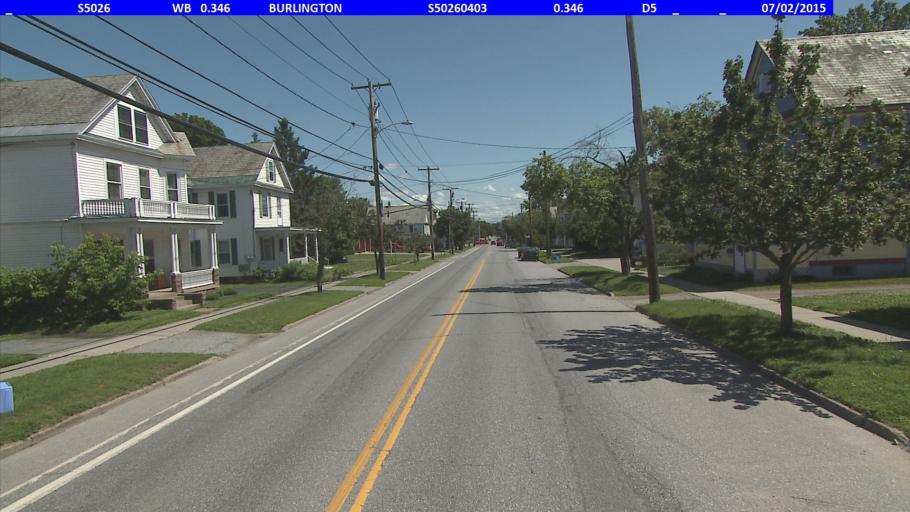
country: US
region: Vermont
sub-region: Chittenden County
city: Burlington
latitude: 44.4862
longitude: -73.2237
